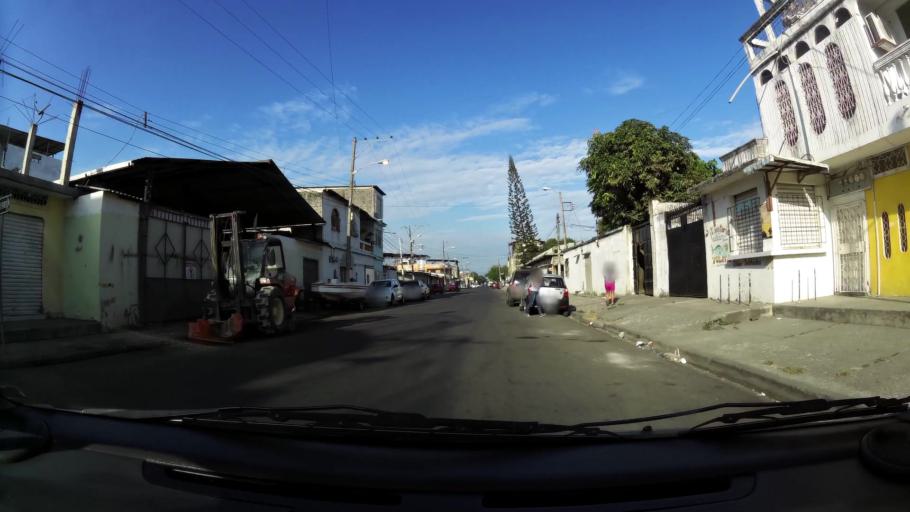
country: EC
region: Guayas
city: Guayaquil
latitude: -2.2268
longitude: -79.9076
